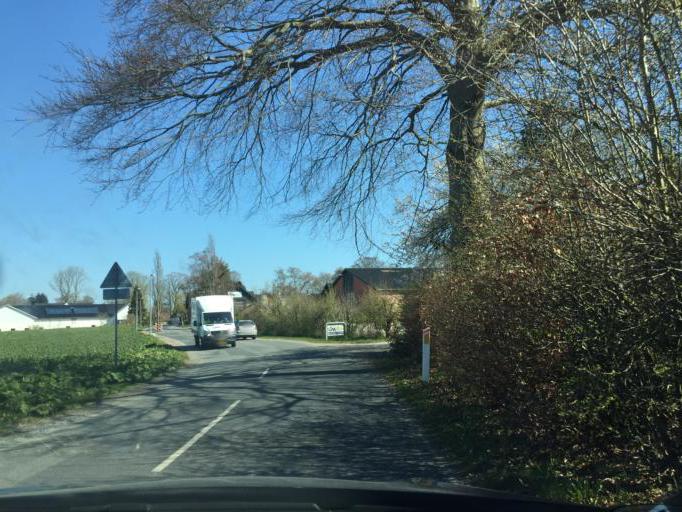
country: DK
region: South Denmark
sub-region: Faaborg-Midtfyn Kommune
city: Ringe
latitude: 55.2490
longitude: 10.5020
